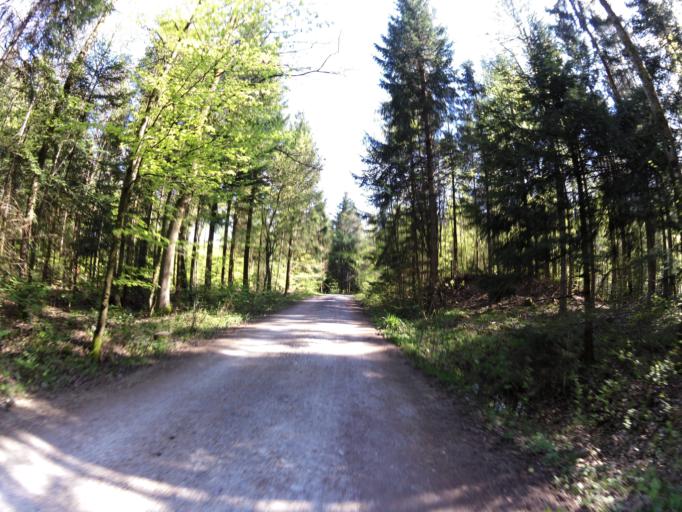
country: CH
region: Aargau
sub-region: Bezirk Aarau
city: Kuttigen
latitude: 47.4066
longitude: 8.0302
